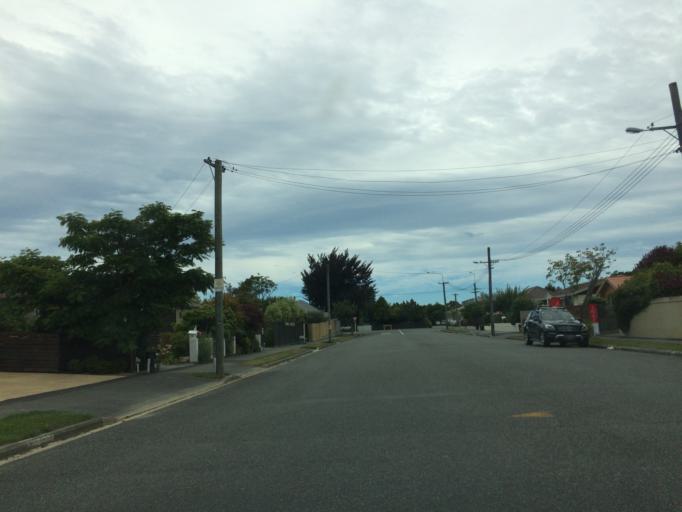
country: NZ
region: Canterbury
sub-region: Christchurch City
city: Christchurch
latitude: -43.5208
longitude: 172.5604
